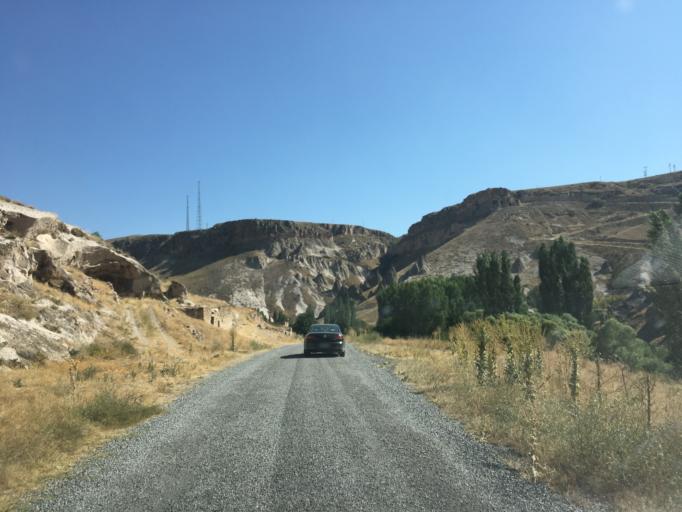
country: TR
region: Kayseri
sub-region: Yesilhisar
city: Yesilhisar
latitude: 38.3474
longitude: 34.9705
